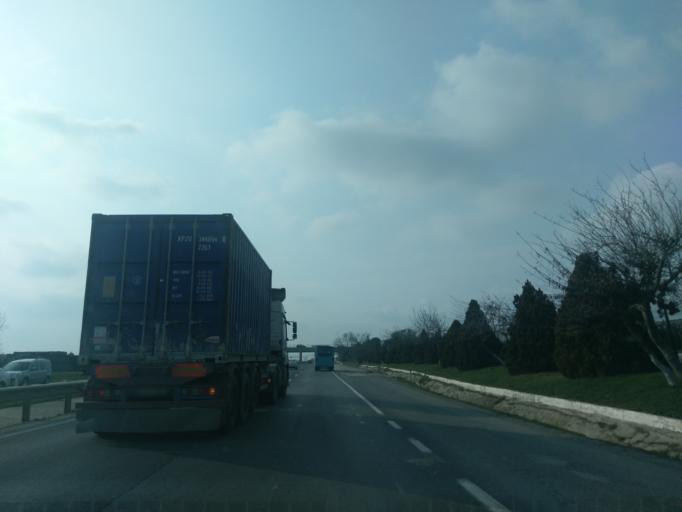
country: TR
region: Istanbul
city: Kavakli
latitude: 41.0680
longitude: 28.3006
